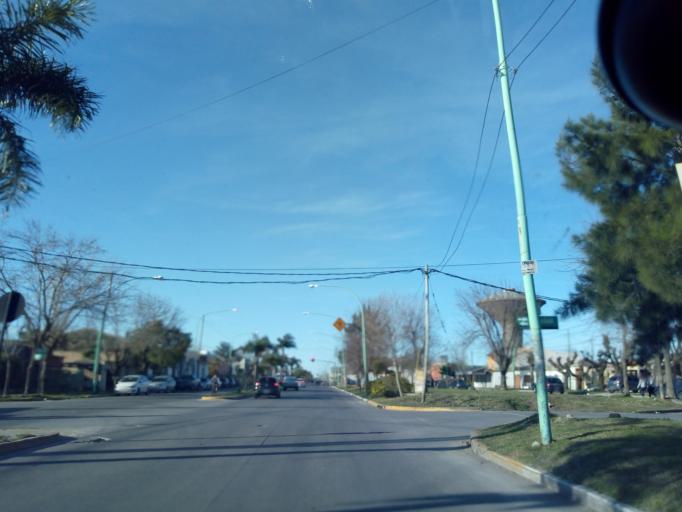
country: AR
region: Buenos Aires
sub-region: Partido de Ensenada
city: Ensenada
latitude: -34.8708
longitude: -57.9118
